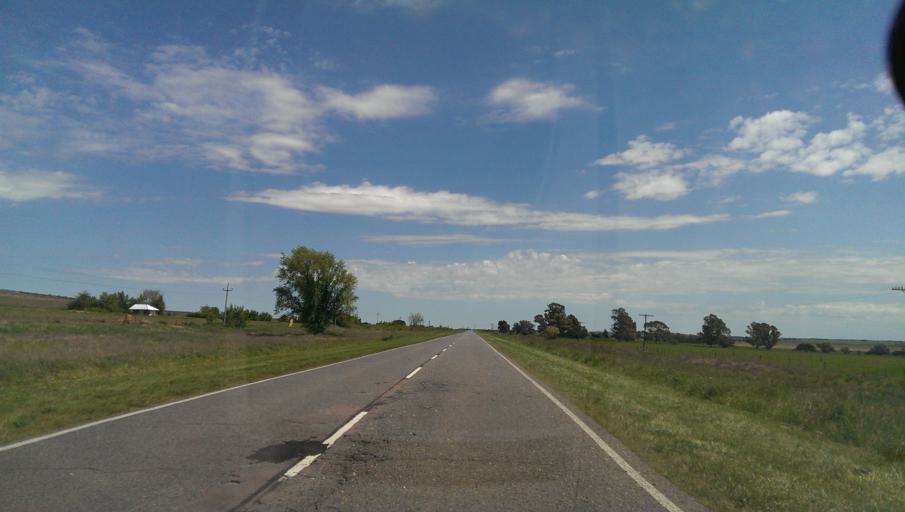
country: AR
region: Buenos Aires
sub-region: Partido de Tornquist
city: Tornquist
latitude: -38.0567
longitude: -62.1857
